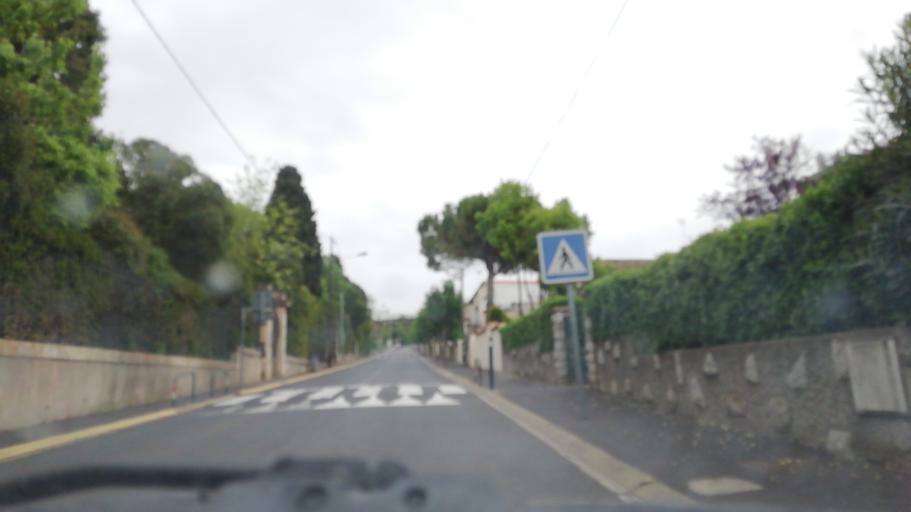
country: FR
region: Languedoc-Roussillon
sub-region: Departement de l'Herault
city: Boujan-sur-Libron
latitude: 43.3702
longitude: 3.2516
